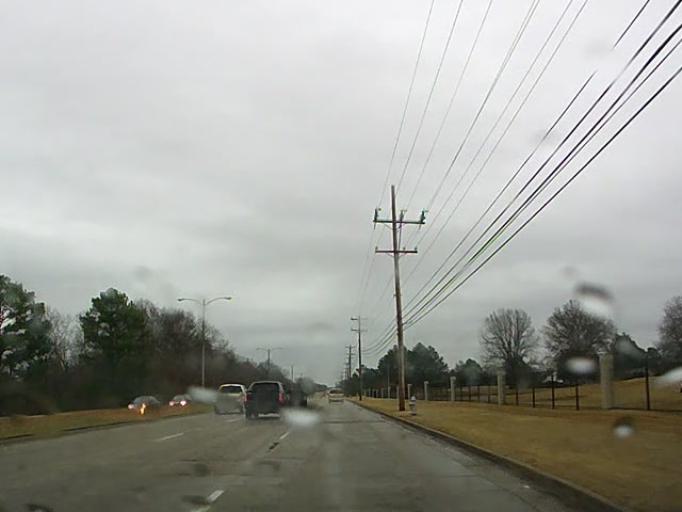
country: US
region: Tennessee
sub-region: Shelby County
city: Germantown
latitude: 35.0479
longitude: -89.7803
